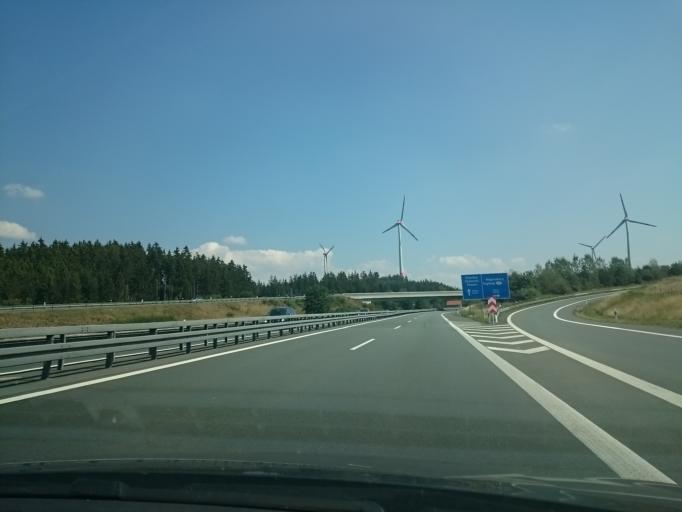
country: DE
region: Bavaria
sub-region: Upper Franconia
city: Trogen
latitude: 50.3815
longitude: 11.9567
